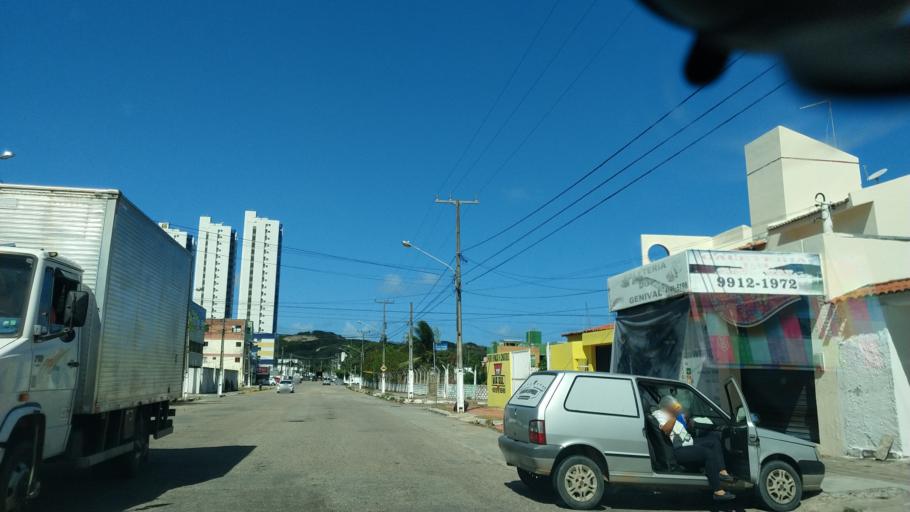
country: BR
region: Rio Grande do Norte
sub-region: Natal
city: Natal
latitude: -5.8699
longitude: -35.1876
